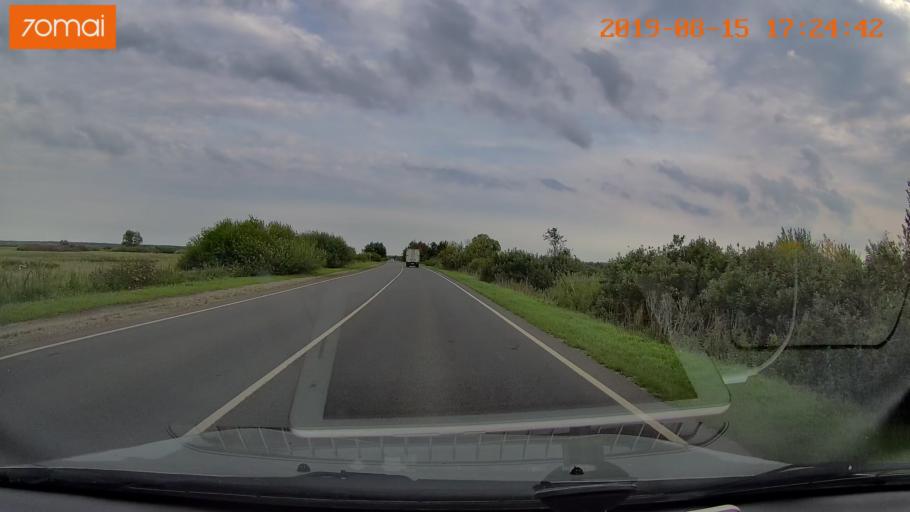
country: RU
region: Moskovskaya
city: Ashitkovo
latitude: 55.3836
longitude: 38.5571
